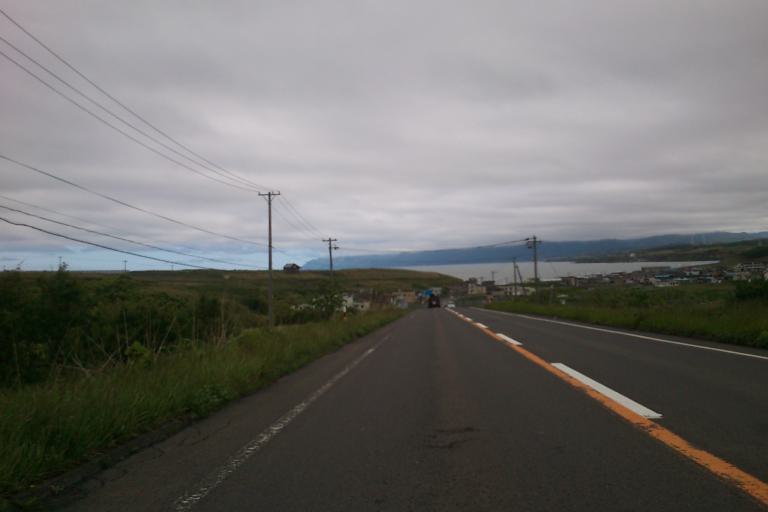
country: JP
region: Hokkaido
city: Ishikari
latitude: 43.3076
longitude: 141.4123
